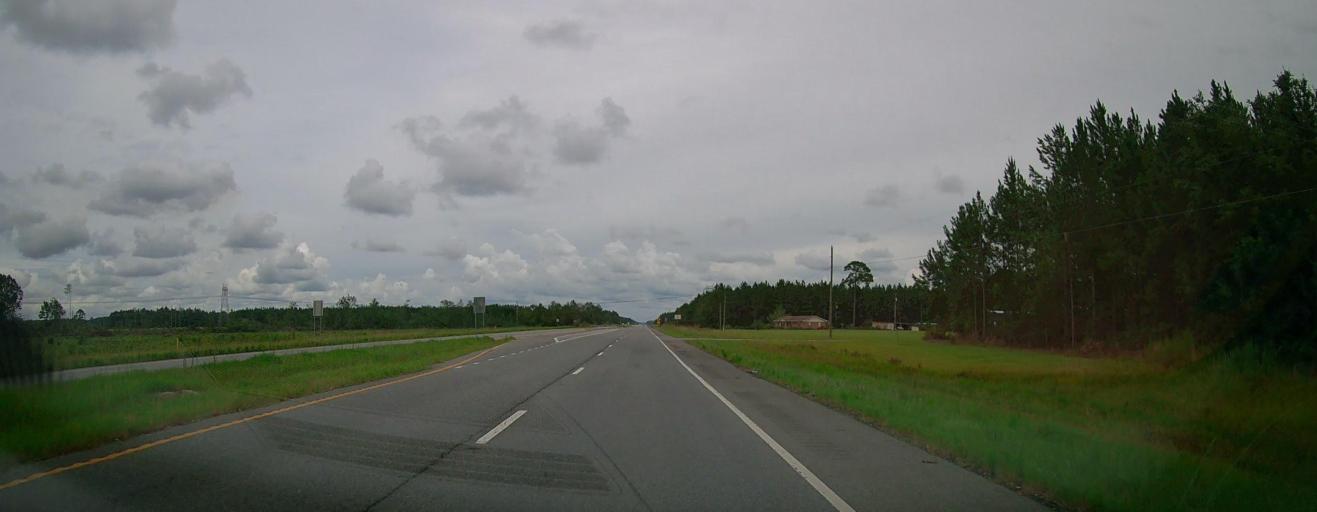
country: US
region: Georgia
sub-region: Appling County
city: Baxley
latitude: 31.7579
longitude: -82.2892
